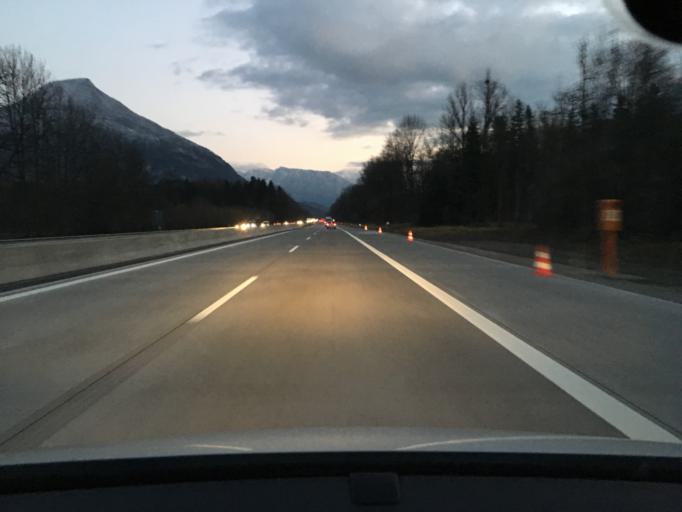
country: DE
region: Bavaria
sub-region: Upper Bavaria
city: Flintsbach
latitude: 47.7216
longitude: 12.1407
